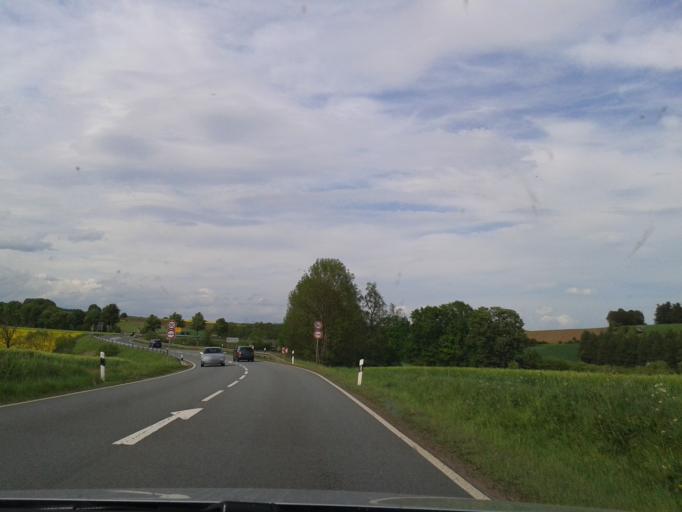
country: DE
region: Hesse
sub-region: Regierungsbezirk Kassel
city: Korbach
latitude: 51.2460
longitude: 8.8953
